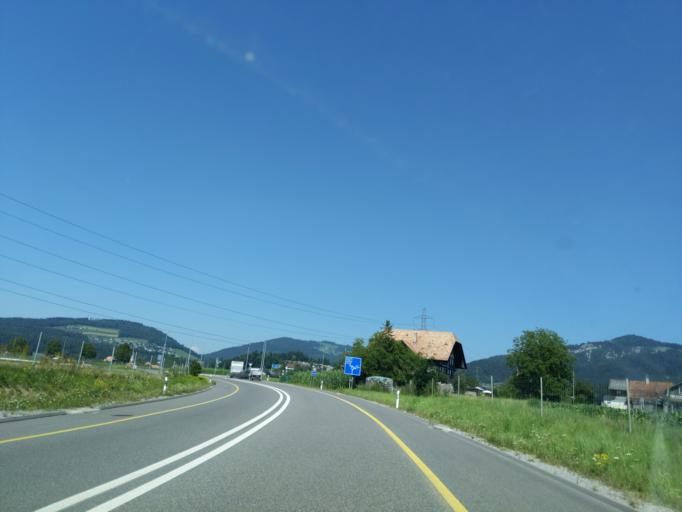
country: CH
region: Bern
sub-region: Thun District
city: Heimberg
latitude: 46.8117
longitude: 7.5913
